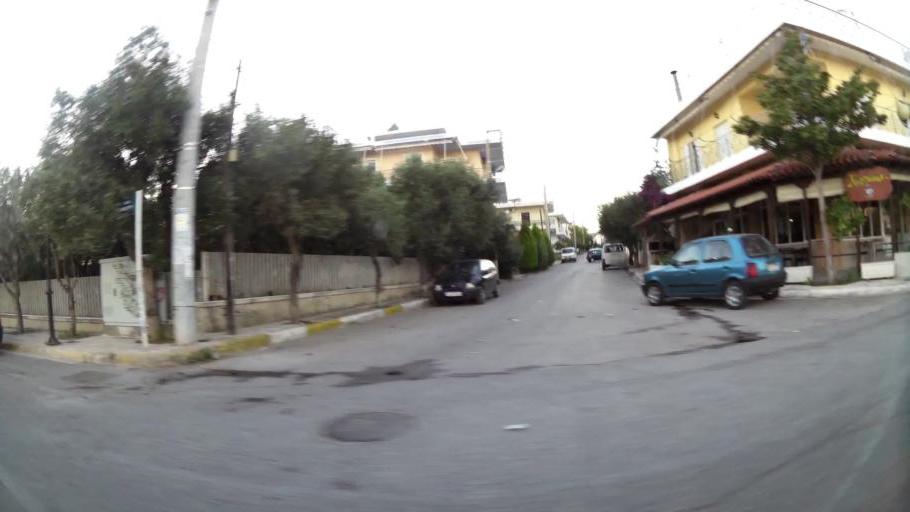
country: GR
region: Attica
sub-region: Nomarchia Dytikis Attikis
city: Ano Liosia
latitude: 38.0887
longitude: 23.7091
